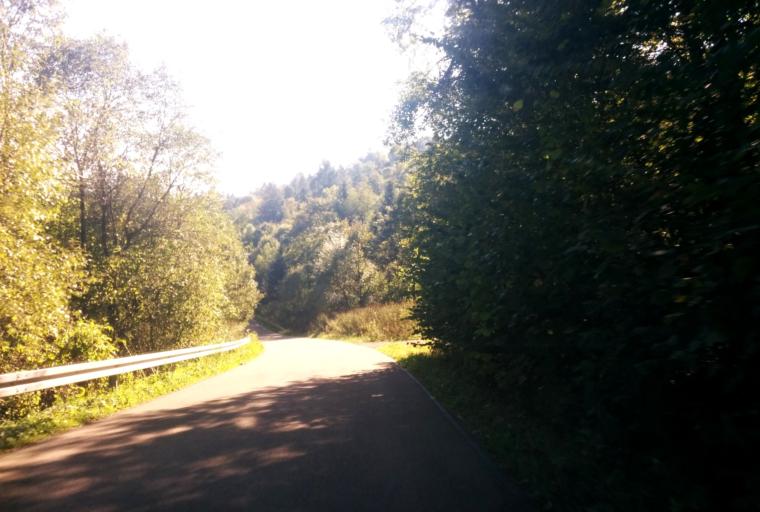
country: PL
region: Subcarpathian Voivodeship
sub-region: Powiat leski
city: Cisna
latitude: 49.2701
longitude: 22.4001
